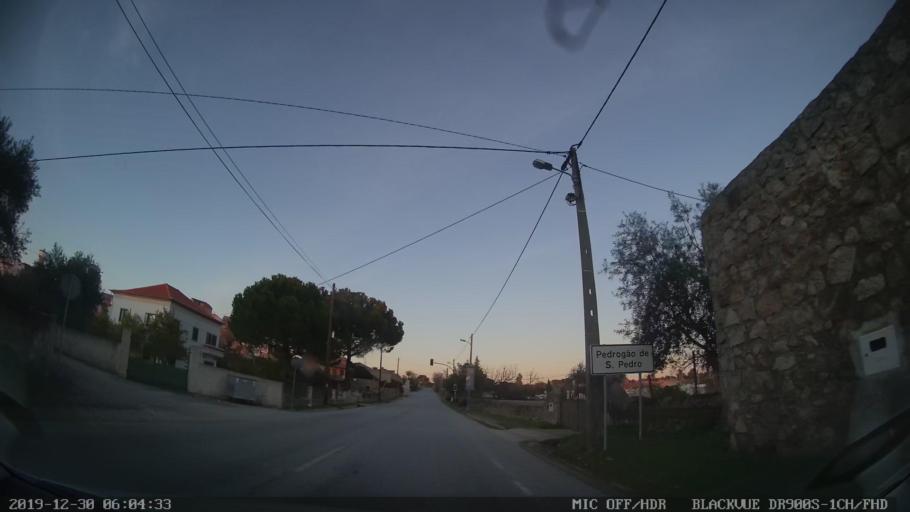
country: PT
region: Castelo Branco
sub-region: Penamacor
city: Penamacor
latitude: 40.0851
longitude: -7.2376
